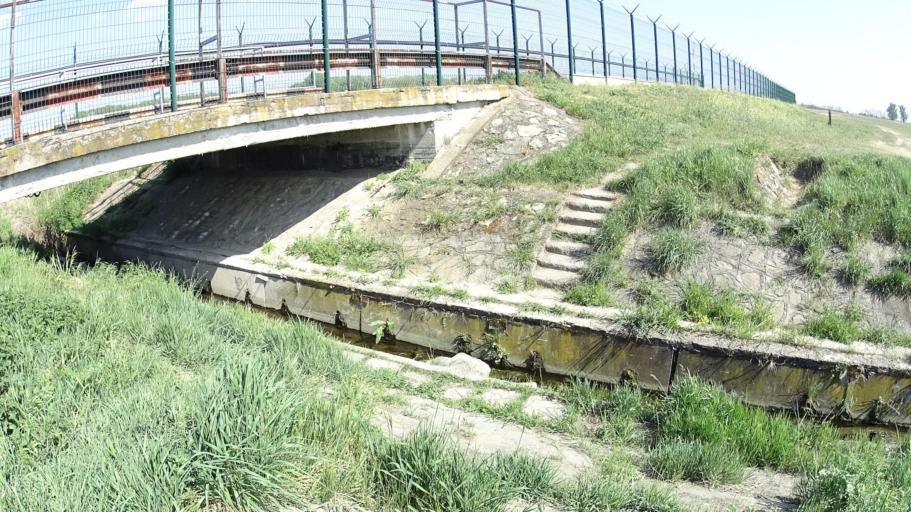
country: HU
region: Pest
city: Vecses
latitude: 47.4171
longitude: 19.3024
